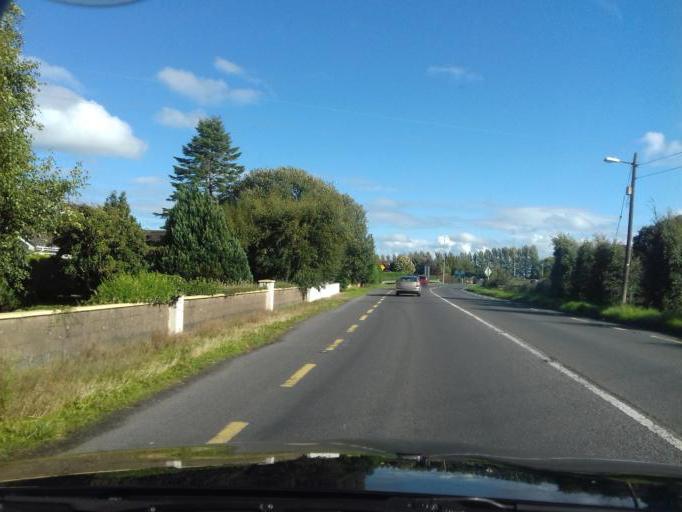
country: IE
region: Leinster
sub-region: Uibh Fhaili
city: Tullamore
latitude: 53.2556
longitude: -7.4810
